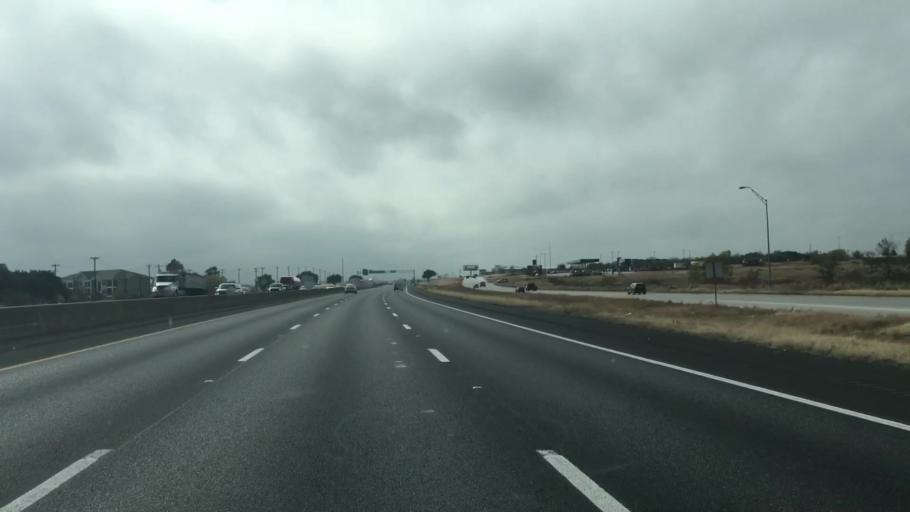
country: US
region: Texas
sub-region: Hays County
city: Kyle
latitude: 30.0312
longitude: -97.8481
